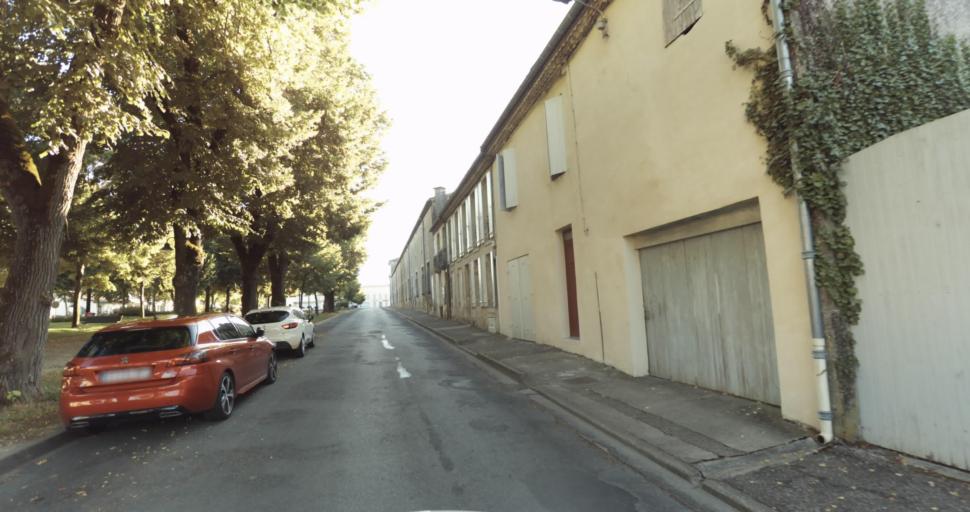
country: FR
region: Aquitaine
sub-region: Departement de la Gironde
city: Bazas
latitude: 44.4324
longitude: -0.2161
